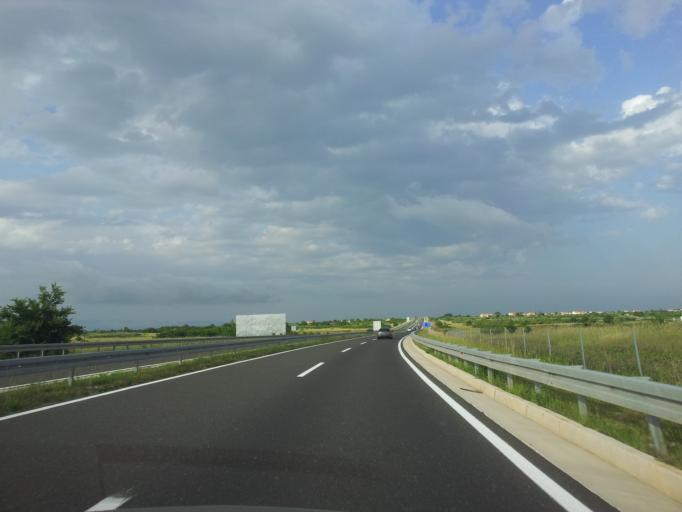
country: HR
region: Zadarska
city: Galovac
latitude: 44.1137
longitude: 15.4041
